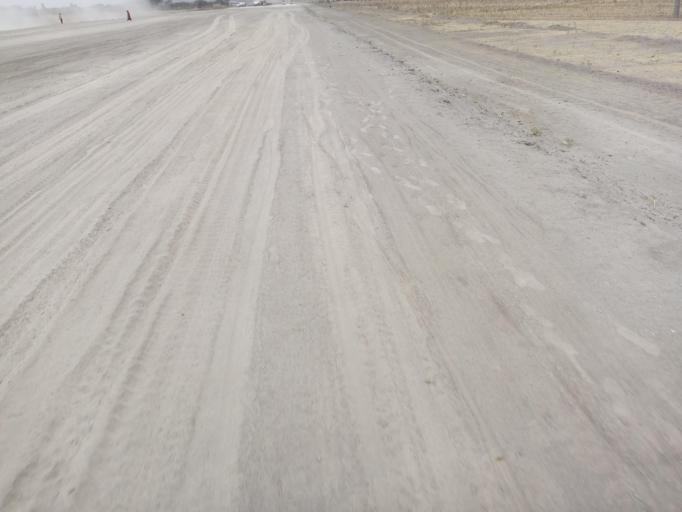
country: ET
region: Oromiya
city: Ziway
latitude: 7.8380
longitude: 38.6546
